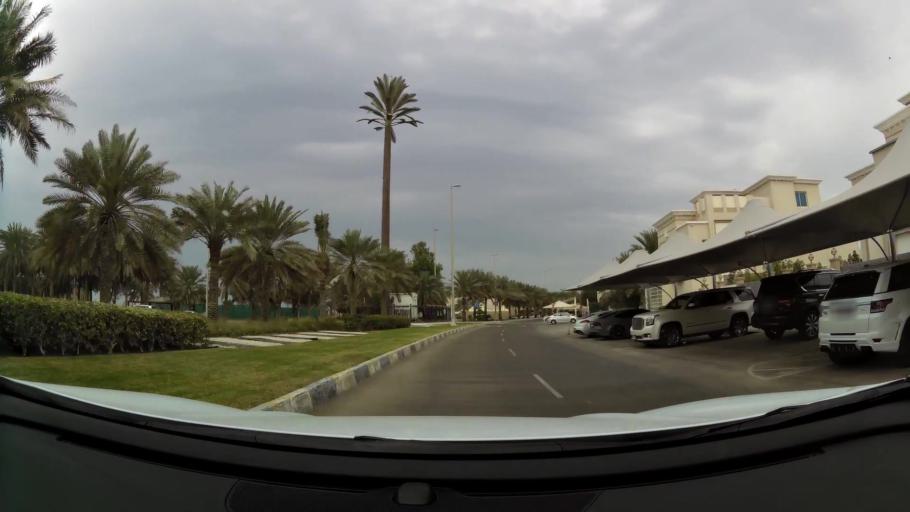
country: AE
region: Abu Dhabi
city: Abu Dhabi
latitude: 24.4778
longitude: 54.3124
